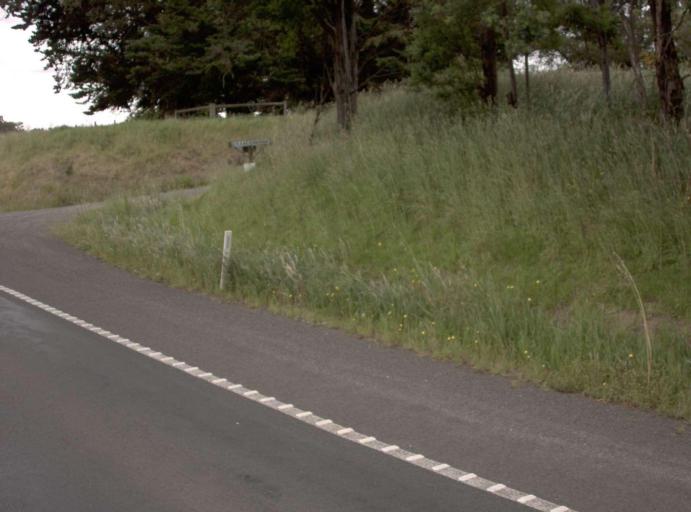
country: AU
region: Victoria
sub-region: Baw Baw
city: Warragul
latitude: -38.4487
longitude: 145.9198
